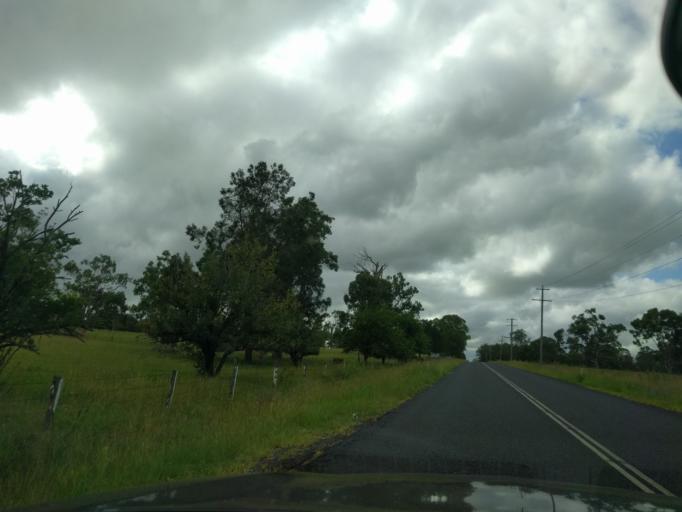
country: AU
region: Queensland
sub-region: Logan
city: Cedar Vale
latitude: -28.0003
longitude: 152.9880
